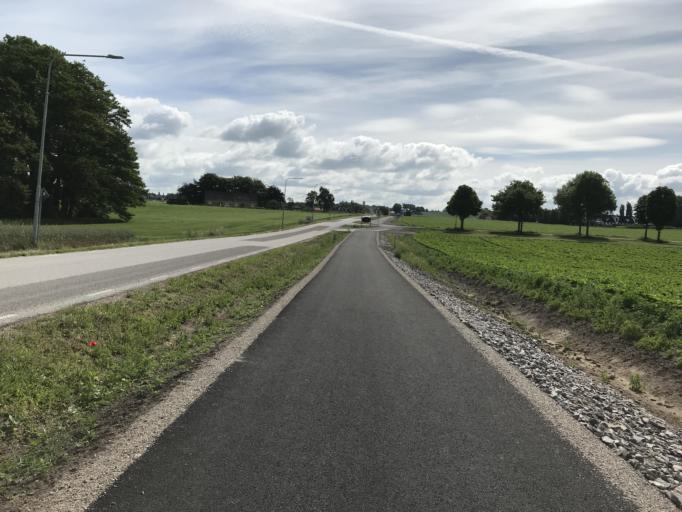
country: SE
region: Skane
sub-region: Helsingborg
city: Rydeback
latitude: 55.9439
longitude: 12.7812
